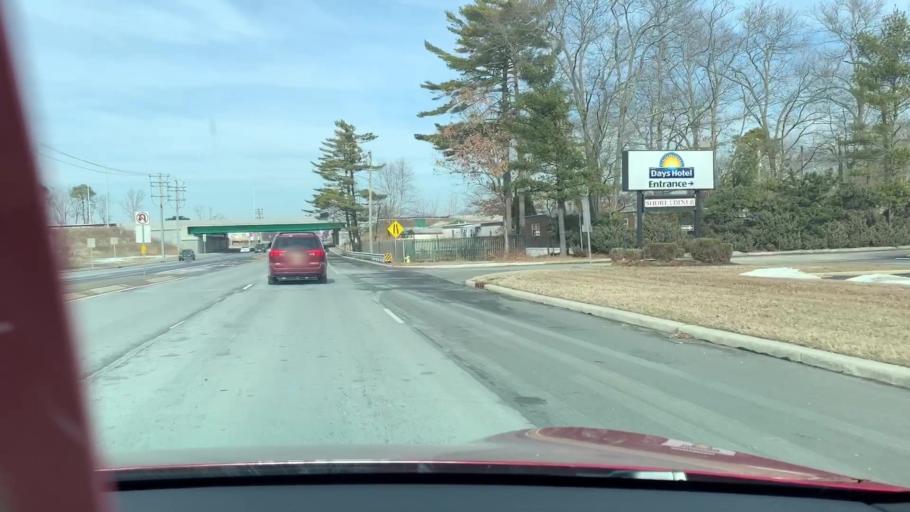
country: US
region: New Jersey
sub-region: Atlantic County
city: Northfield
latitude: 39.3966
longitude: -74.5602
